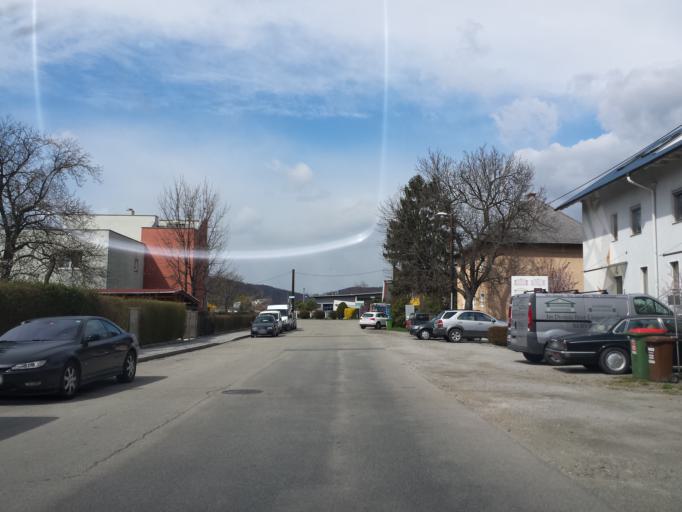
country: AT
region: Styria
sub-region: Graz Stadt
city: Goesting
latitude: 47.0833
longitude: 15.4088
